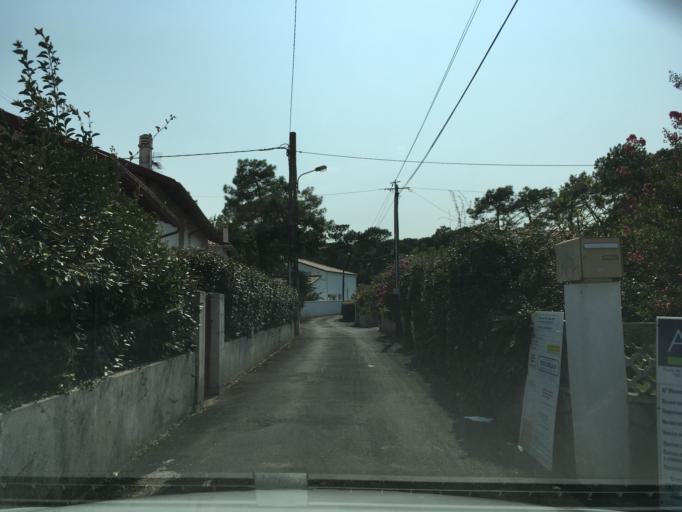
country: FR
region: Aquitaine
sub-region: Departement des Pyrenees-Atlantiques
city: Boucau
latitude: 43.5239
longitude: -1.5086
